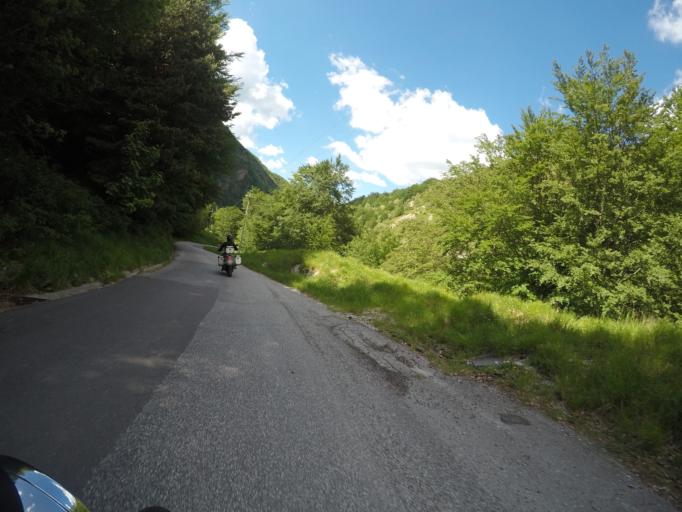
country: IT
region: Tuscany
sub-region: Provincia di Lucca
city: Minucciano
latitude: 44.1392
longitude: 10.1959
